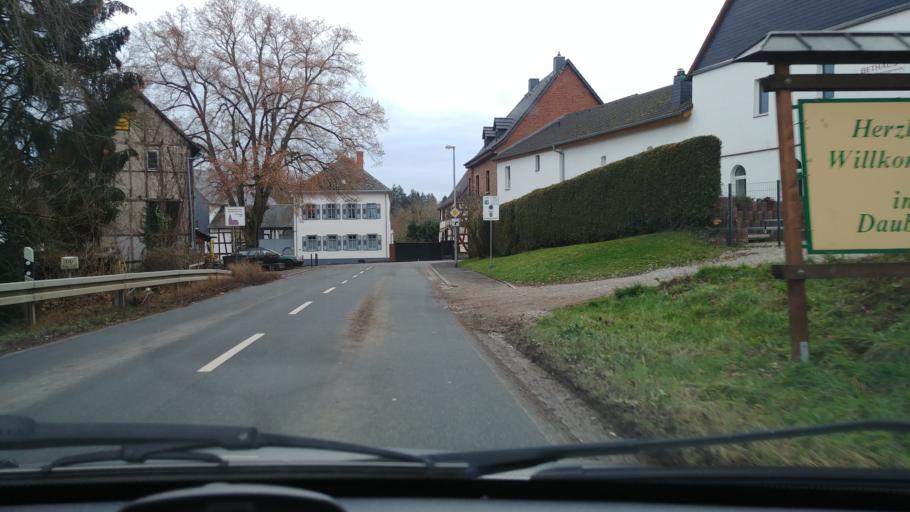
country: DE
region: Hesse
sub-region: Regierungsbezirk Giessen
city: Villmar
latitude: 50.3319
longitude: 8.1782
